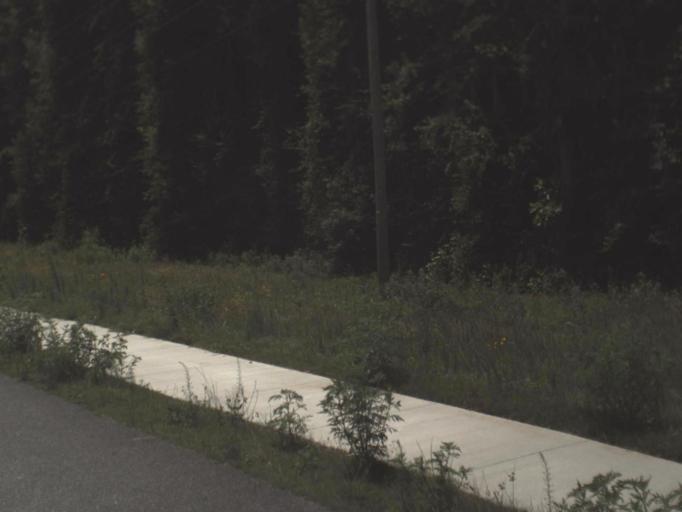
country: US
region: Florida
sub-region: Madison County
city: Madison
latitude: 30.4777
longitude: -83.4375
